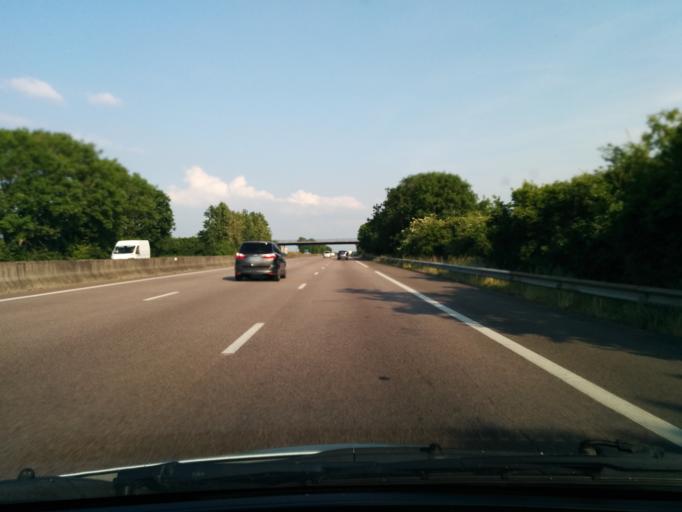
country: FR
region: Haute-Normandie
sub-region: Departement de l'Eure
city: La Chapelle-Reanville
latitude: 49.0748
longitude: 1.3987
